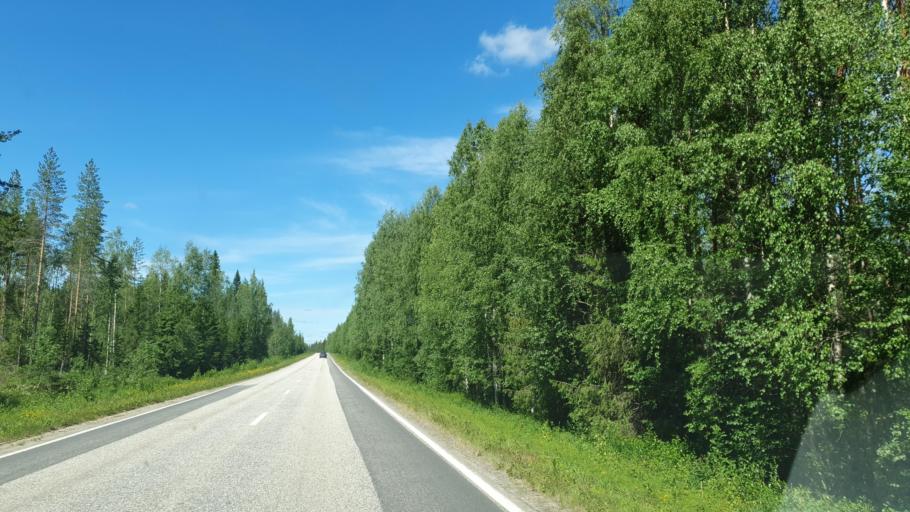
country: FI
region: Kainuu
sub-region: Kehys-Kainuu
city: Hyrynsalmi
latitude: 64.6326
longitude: 28.5918
